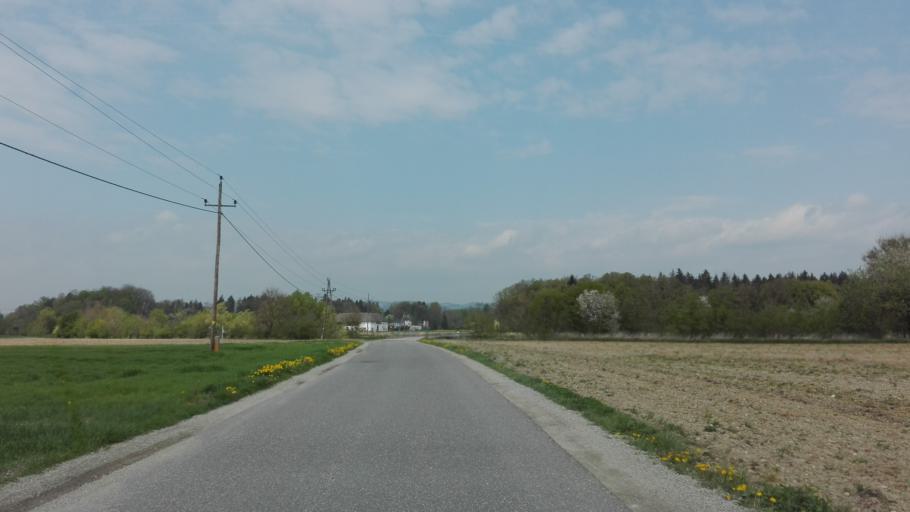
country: AT
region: Upper Austria
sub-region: Politischer Bezirk Perg
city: Perg
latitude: 48.2013
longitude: 14.6898
